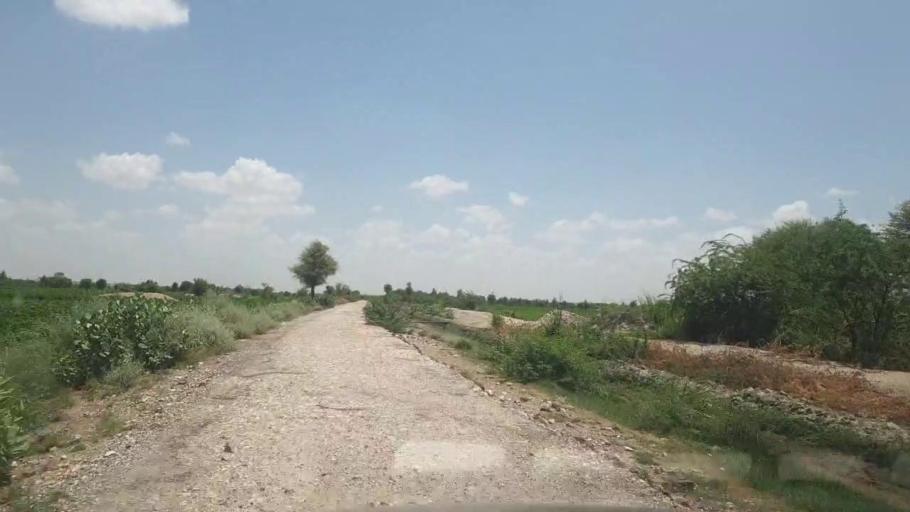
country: PK
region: Sindh
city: Kot Diji
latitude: 27.2922
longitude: 69.0840
